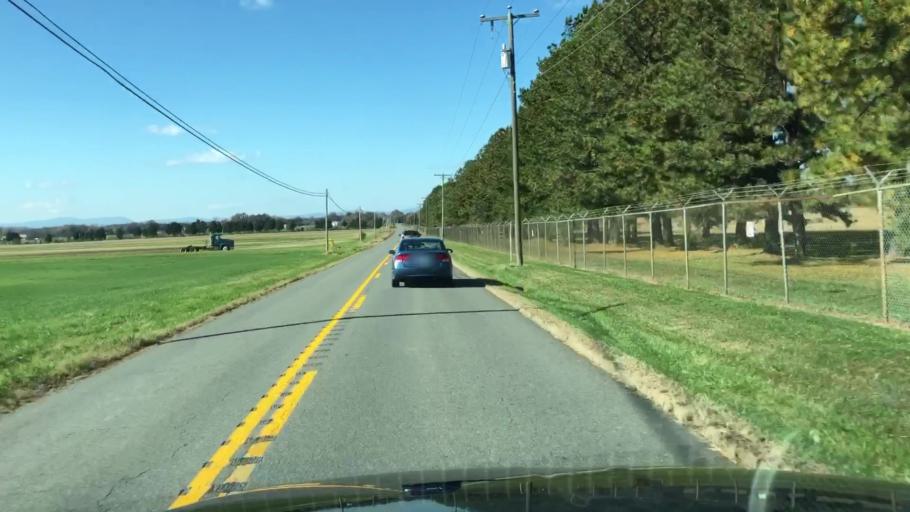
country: US
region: Virginia
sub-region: Fauquier County
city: Bealeton
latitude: 38.5154
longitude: -77.7868
